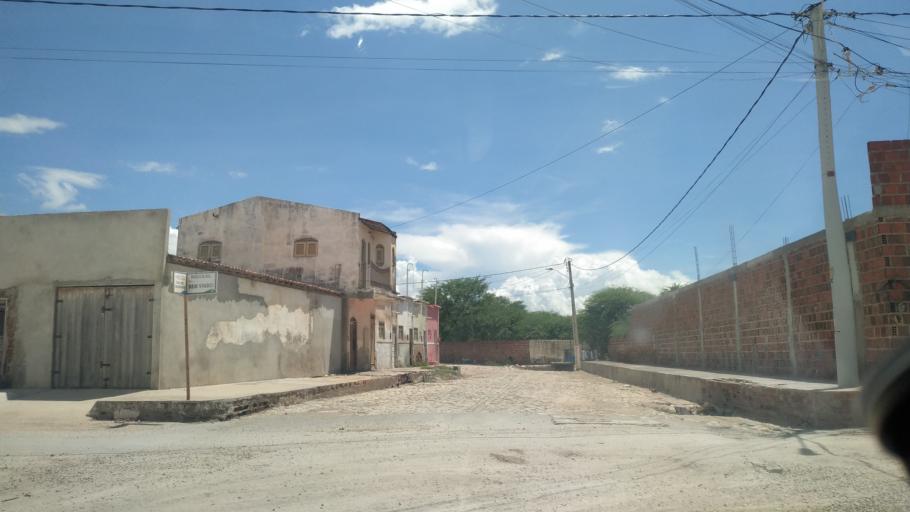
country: BR
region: Rio Grande do Norte
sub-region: Areia Branca
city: Areia Branca
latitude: -4.9508
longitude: -37.1335
